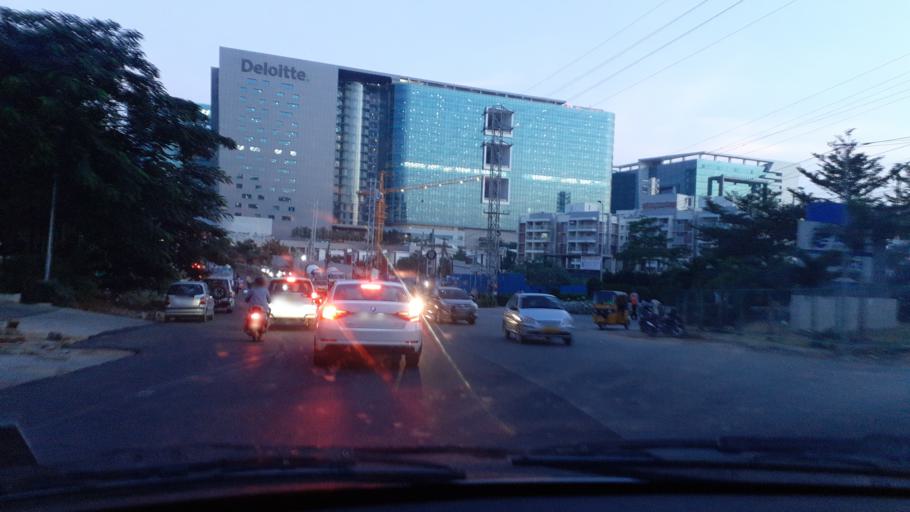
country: IN
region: Telangana
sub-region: Rangareddi
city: Kukatpalli
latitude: 17.4442
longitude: 78.3670
